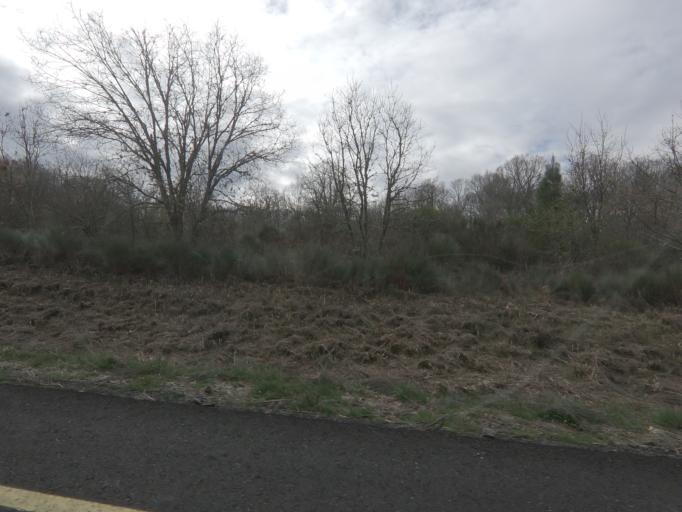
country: ES
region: Castille and Leon
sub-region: Provincia de Salamanca
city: Penaparda
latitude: 40.2785
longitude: -6.6779
